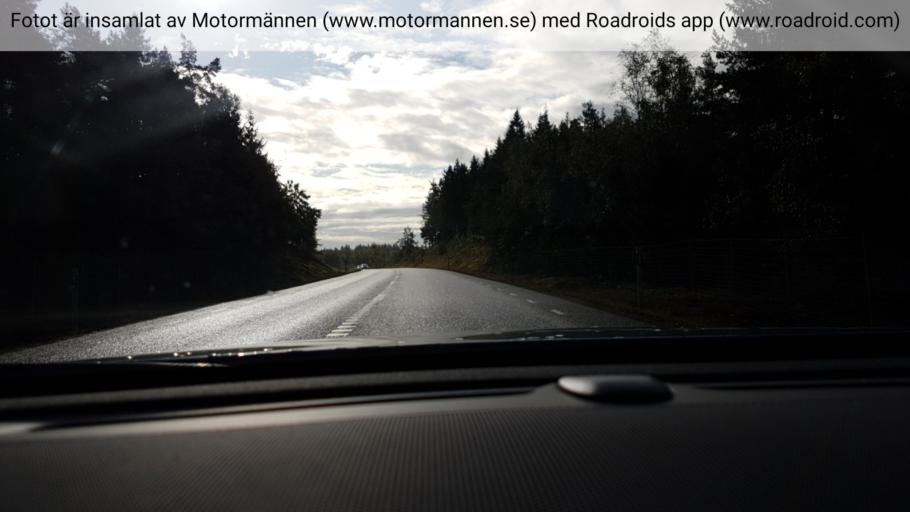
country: SE
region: Vaestra Goetaland
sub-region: Harryda Kommun
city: Hindas
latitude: 57.6578
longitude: 12.3730
